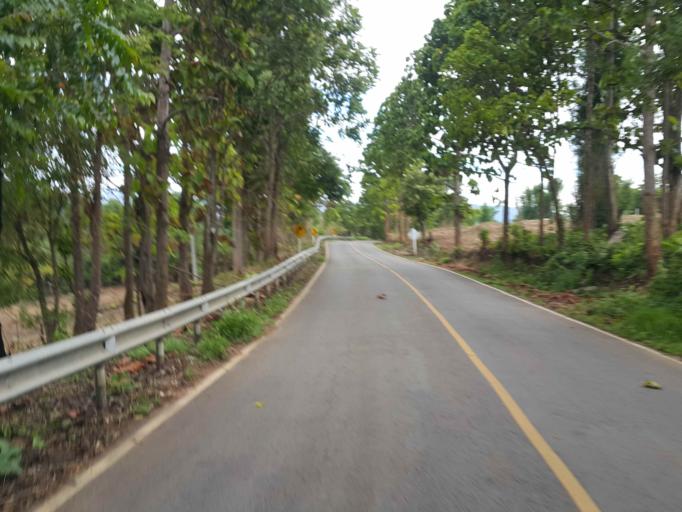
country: TH
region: Chiang Mai
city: Mae Chaem
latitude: 18.4956
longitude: 98.3888
